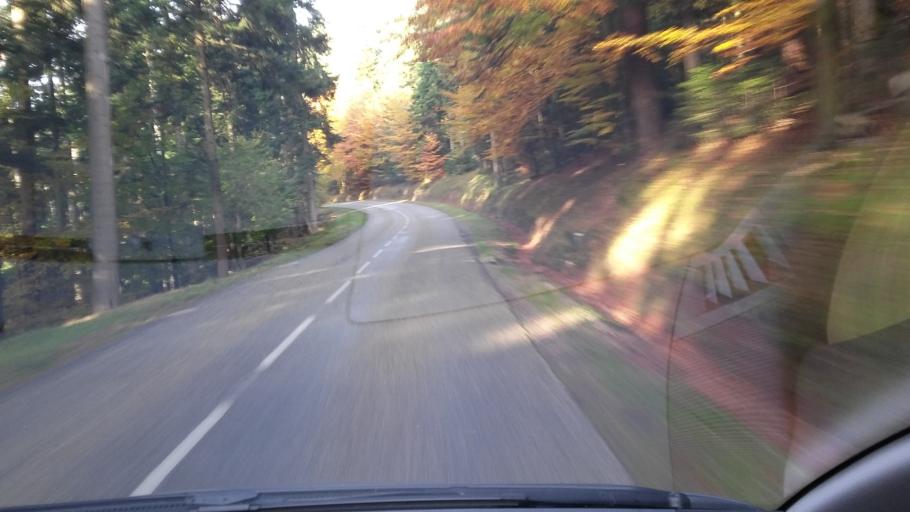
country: FR
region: Lorraine
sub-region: Departement de la Moselle
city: Dabo
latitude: 48.6623
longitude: 7.2619
